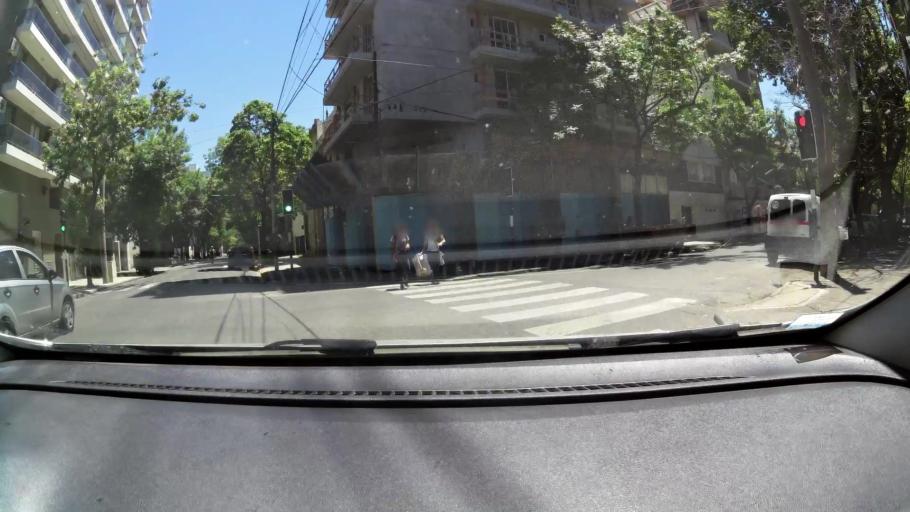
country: AR
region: Santa Fe
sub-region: Departamento de Rosario
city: Rosario
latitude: -32.9462
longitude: -60.6609
